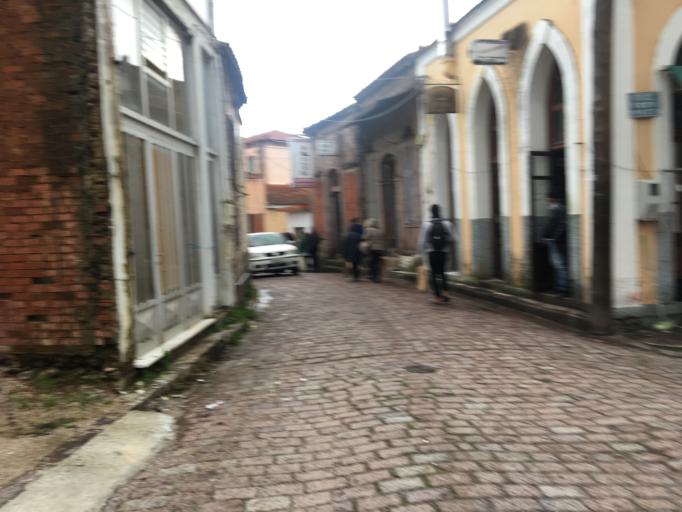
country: GR
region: North Aegean
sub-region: Nomos Lesvou
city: Agia Paraskevi
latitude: 39.2480
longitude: 26.2715
